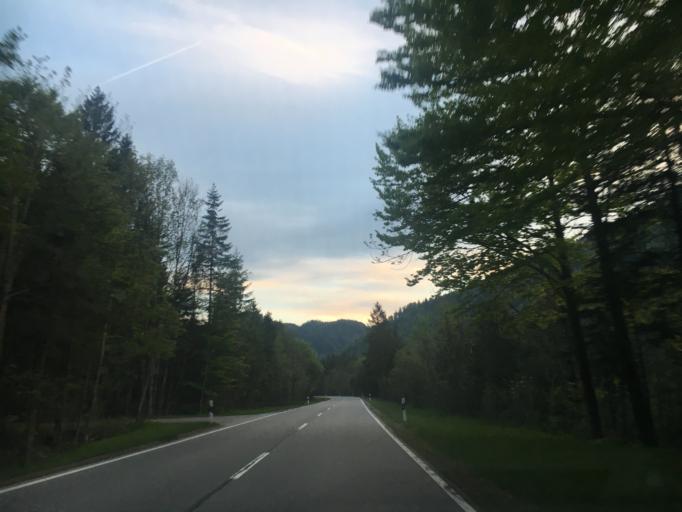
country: DE
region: Bavaria
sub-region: Upper Bavaria
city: Lenggries
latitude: 47.5975
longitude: 11.5636
